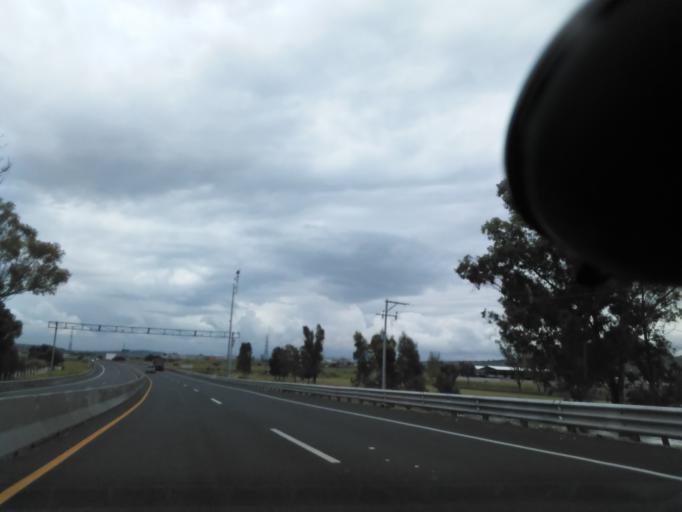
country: MX
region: Mexico
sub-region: Huehuetoca
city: Casa Nueva
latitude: 19.8239
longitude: -99.2193
